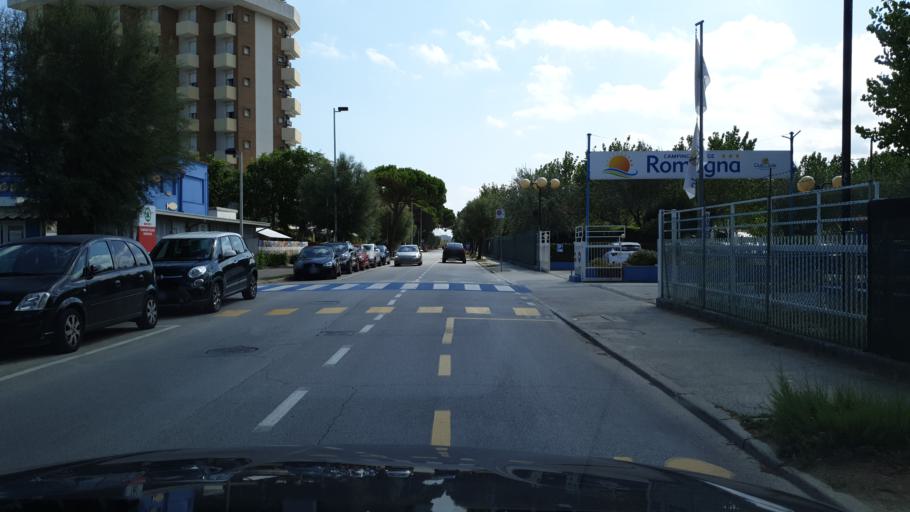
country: IT
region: Emilia-Romagna
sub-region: Provincia di Rimini
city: Misano Adriatico
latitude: 43.9896
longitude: 12.6815
